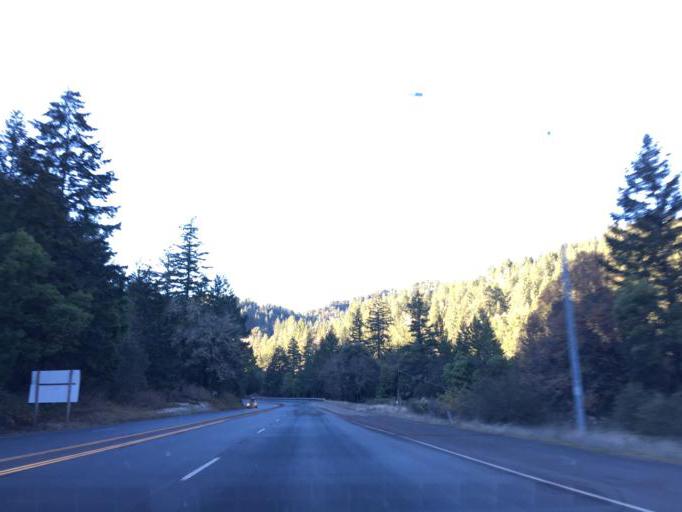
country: US
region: California
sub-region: Mendocino County
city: Laytonville
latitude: 39.8276
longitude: -123.5969
